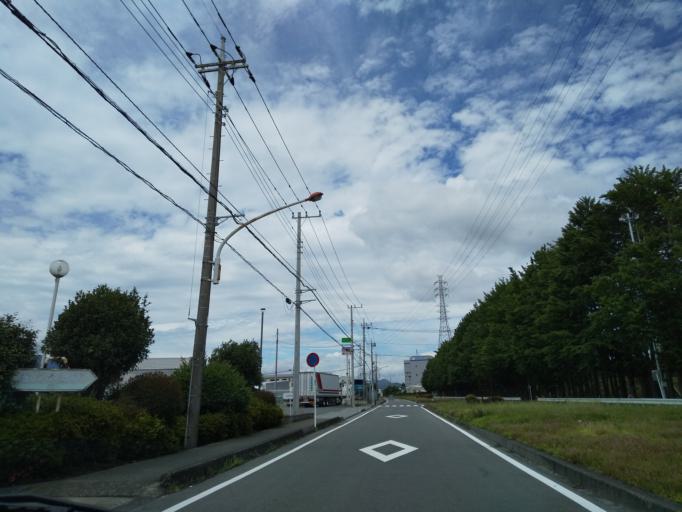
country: JP
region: Kanagawa
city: Zama
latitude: 35.5089
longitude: 139.3455
